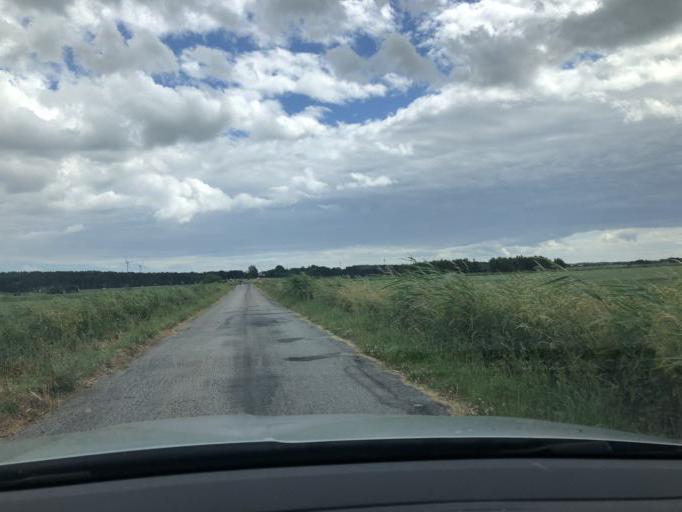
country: SE
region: Blekinge
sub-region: Solvesborgs Kommun
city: Soelvesborg
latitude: 56.0972
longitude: 14.6335
